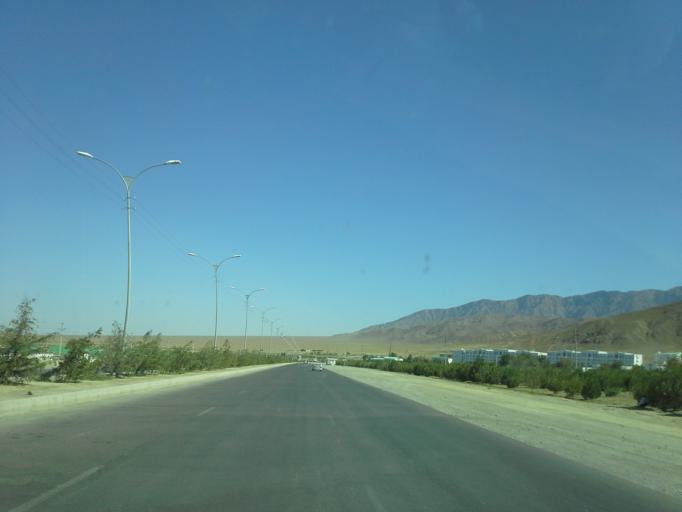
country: TM
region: Ahal
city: Baharly
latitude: 38.5235
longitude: 57.1788
